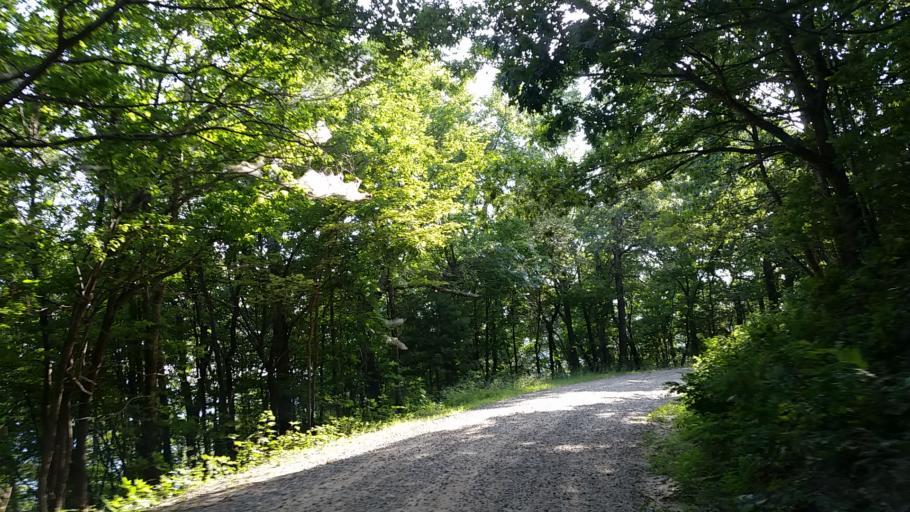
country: US
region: Georgia
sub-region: Lumpkin County
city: Dahlonega
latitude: 34.6381
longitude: -84.0346
